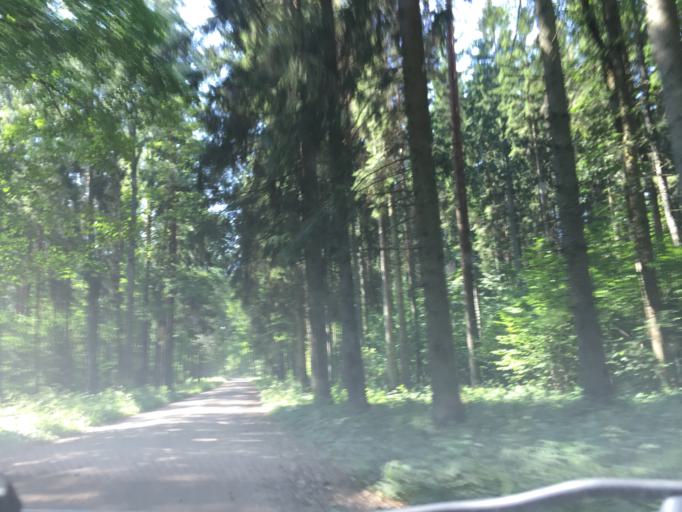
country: LV
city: Tervete
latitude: 56.4847
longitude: 23.3995
